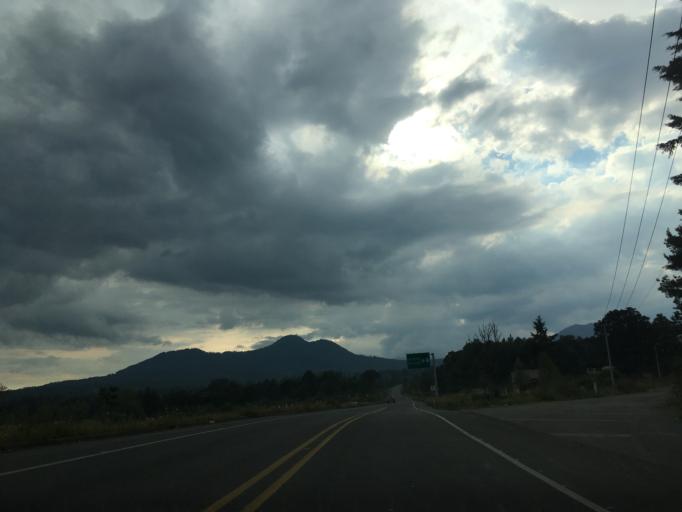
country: MX
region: Michoacan
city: Capacuaro
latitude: 19.5078
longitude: -102.1226
